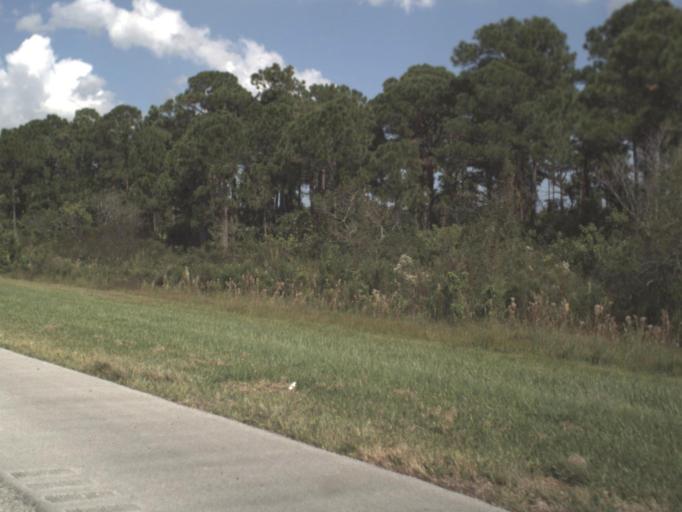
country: US
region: Florida
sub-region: Saint Lucie County
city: Lakewood Park
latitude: 27.4502
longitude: -80.4280
